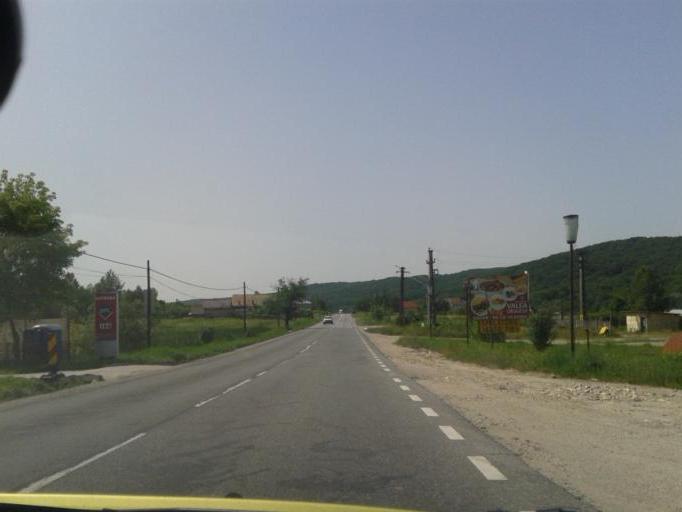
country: RO
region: Arges
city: Draganu-Olteni
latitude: 44.9198
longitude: 24.7212
